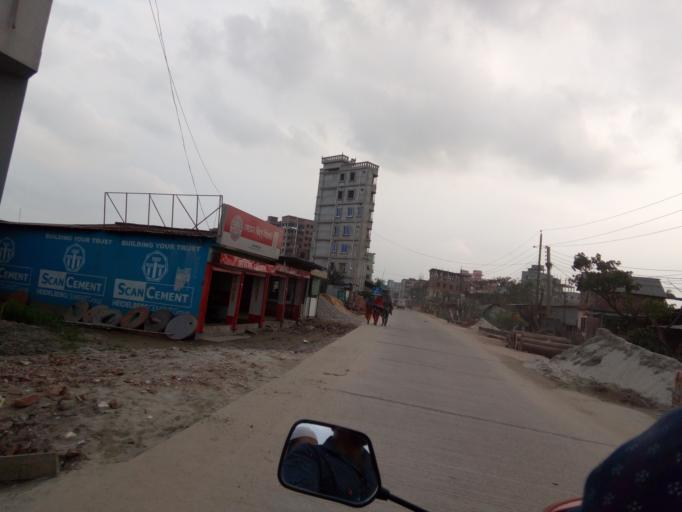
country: BD
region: Dhaka
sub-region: Dhaka
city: Dhaka
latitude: 23.7045
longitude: 90.4692
